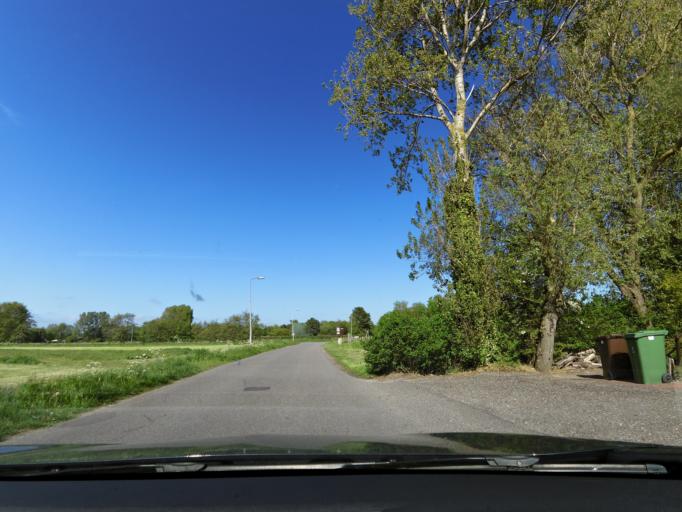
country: NL
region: South Holland
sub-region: Gemeente Goeree-Overflakkee
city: Ouddorp
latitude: 51.8014
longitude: 3.9082
